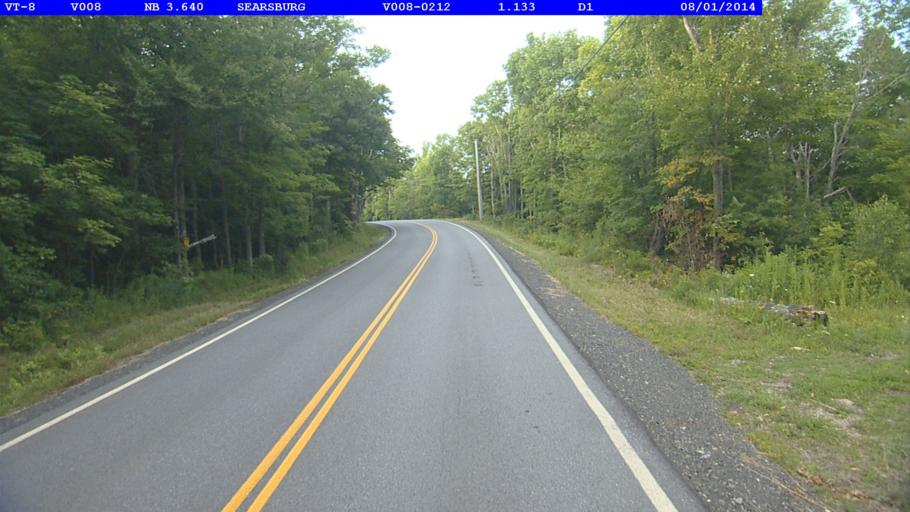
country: US
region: Vermont
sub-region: Windham County
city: Dover
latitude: 42.8734
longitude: -72.9696
